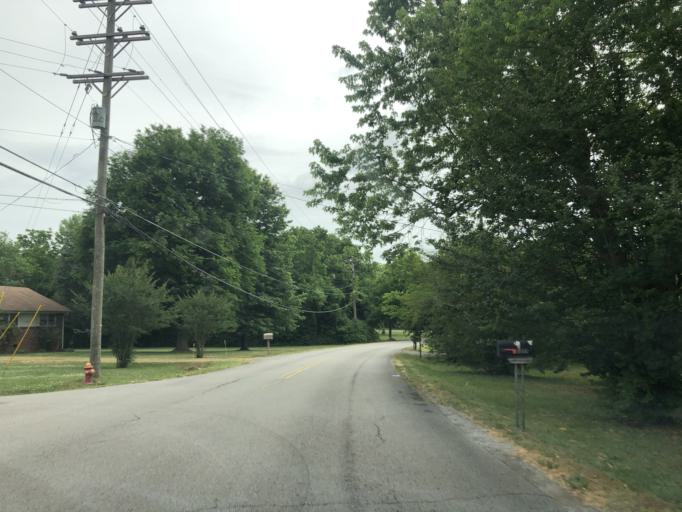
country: US
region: Tennessee
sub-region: Davidson County
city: Goodlettsville
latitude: 36.2621
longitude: -86.7652
